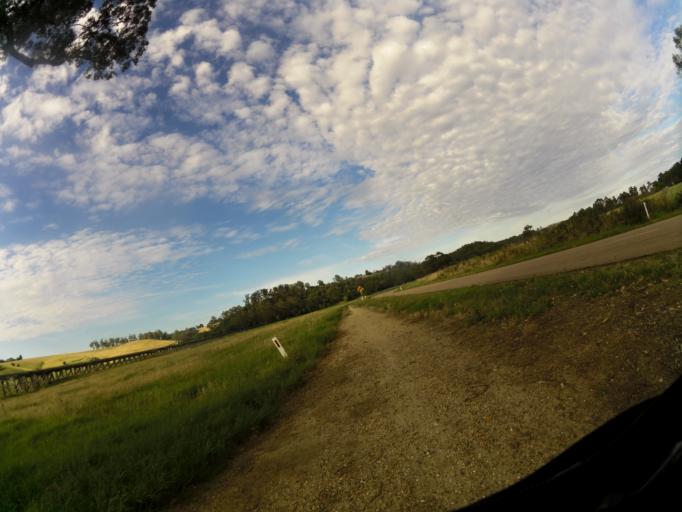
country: AU
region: Victoria
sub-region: East Gippsland
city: Lakes Entrance
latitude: -37.7243
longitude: 148.4469
